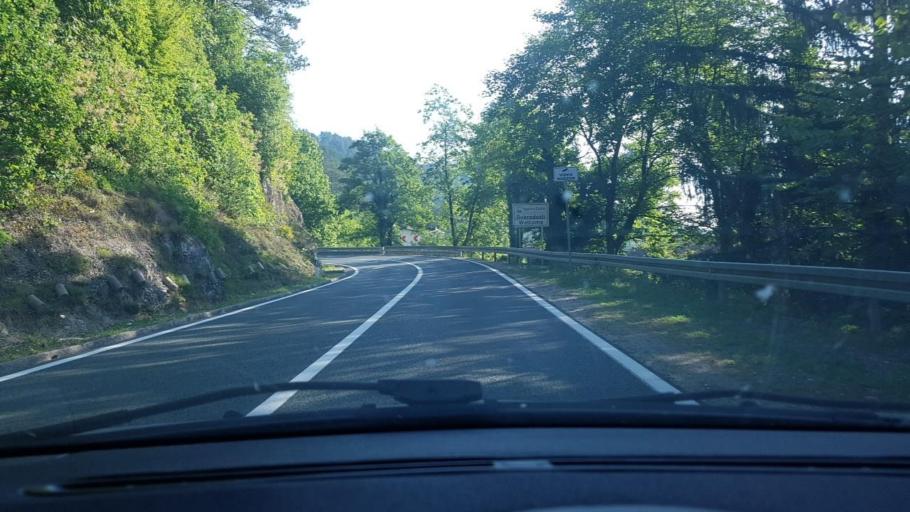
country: BA
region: Federation of Bosnia and Herzegovina
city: Ostrozac
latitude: 44.8993
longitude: 15.9355
